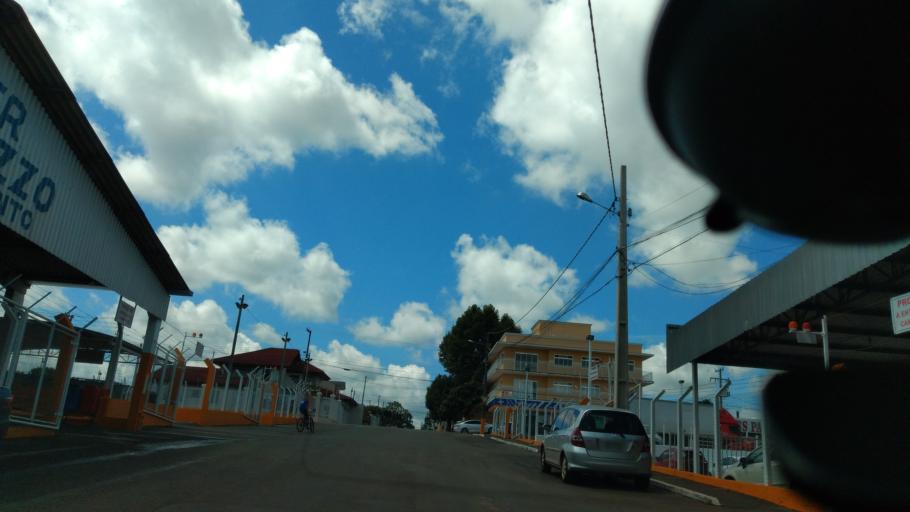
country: BR
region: Parana
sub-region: Guarapuava
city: Guarapuava
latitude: -25.3972
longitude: -51.4963
